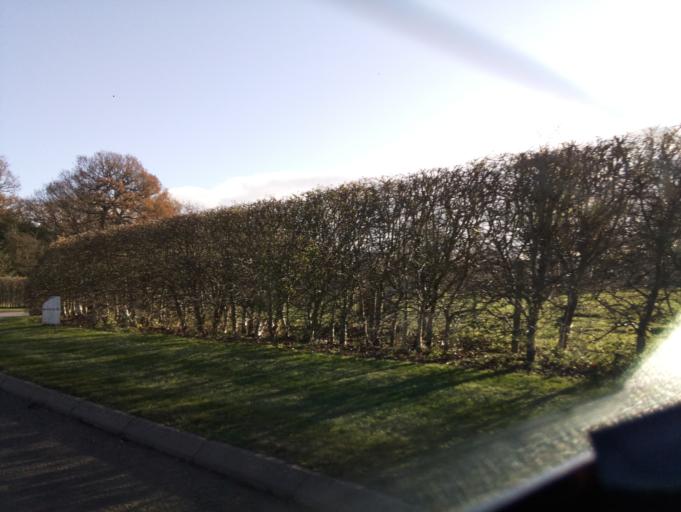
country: GB
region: England
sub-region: Staffordshire
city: Barton under Needwood
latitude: 52.8162
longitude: -1.7440
